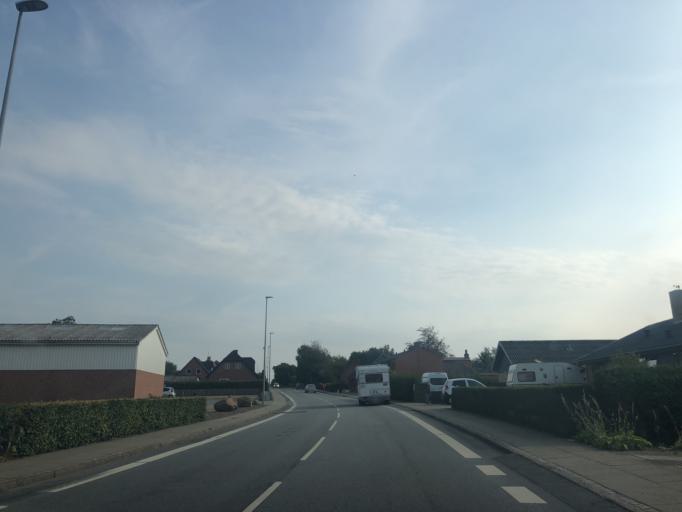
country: DK
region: Central Jutland
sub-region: Skive Kommune
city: Skive
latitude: 56.6214
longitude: 8.8803
